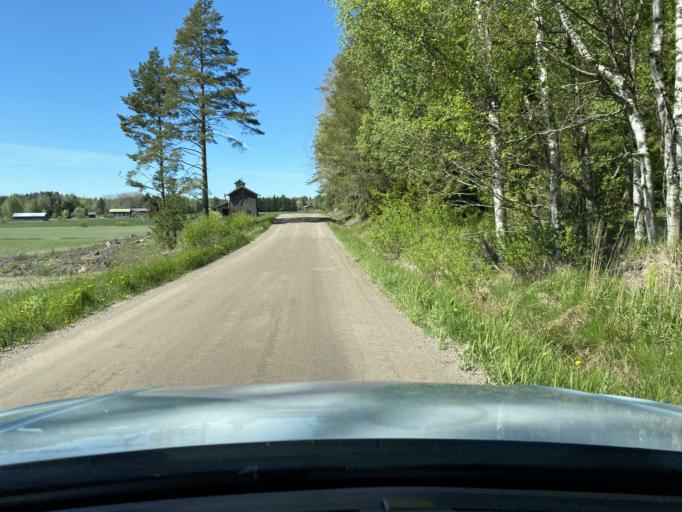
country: FI
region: Satakunta
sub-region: Rauma
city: Lappi
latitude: 61.1370
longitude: 21.9668
